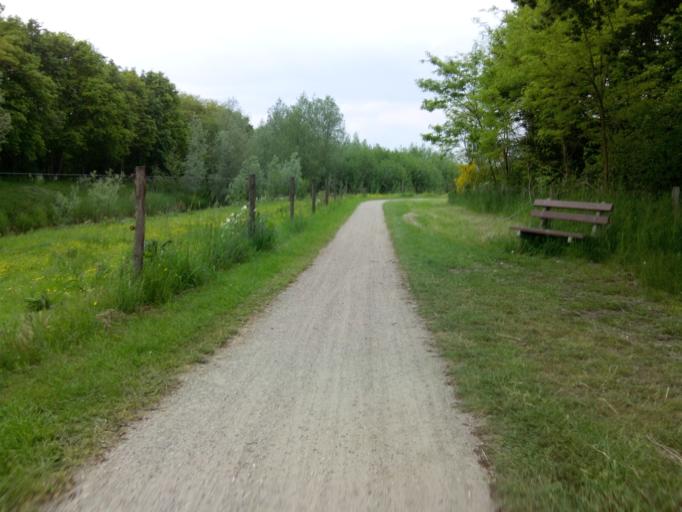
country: NL
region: Gelderland
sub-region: Berkelland
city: Borculo
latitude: 52.0702
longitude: 6.5233
